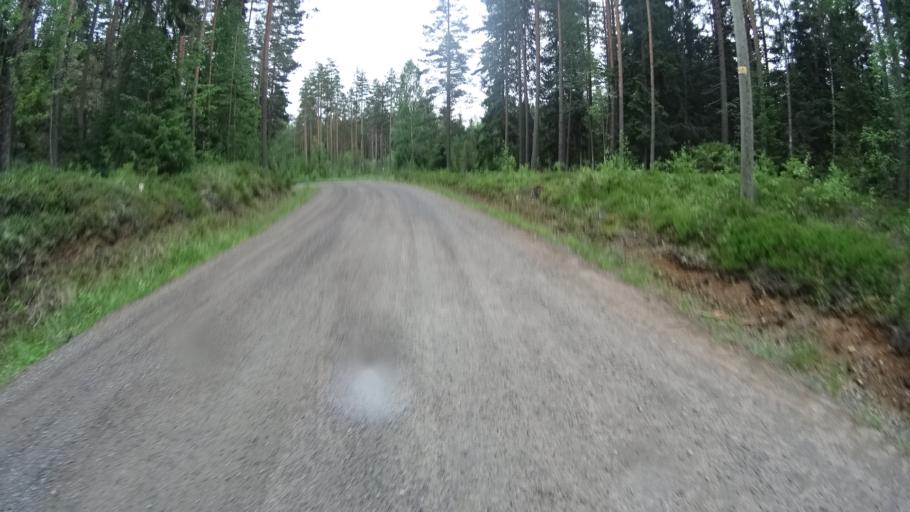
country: FI
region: Uusimaa
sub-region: Helsinki
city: Karkkila
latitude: 60.6025
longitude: 24.1813
